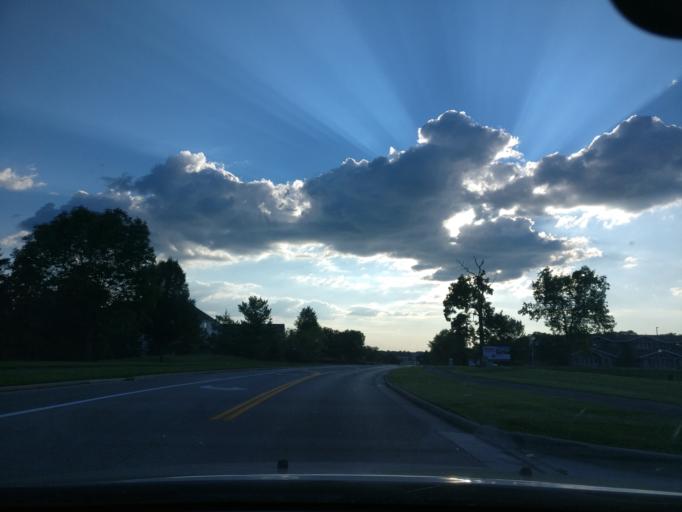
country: US
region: Ohio
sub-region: Warren County
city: Springboro
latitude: 39.5792
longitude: -84.2231
